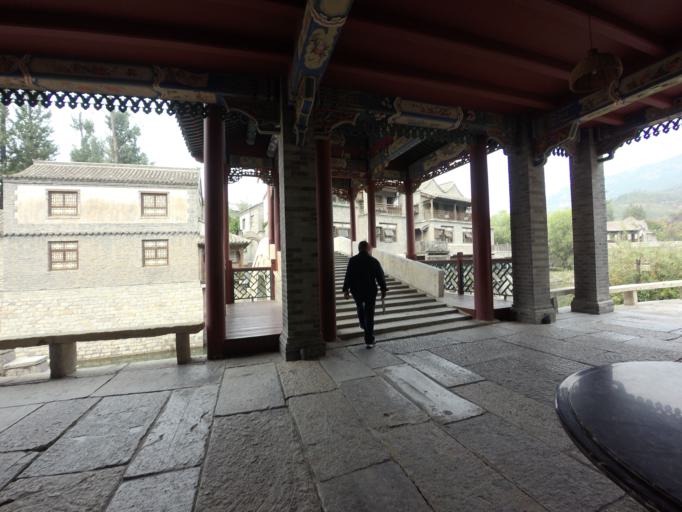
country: CN
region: Beijing
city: Xinchengzi
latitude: 40.6513
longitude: 117.2714
